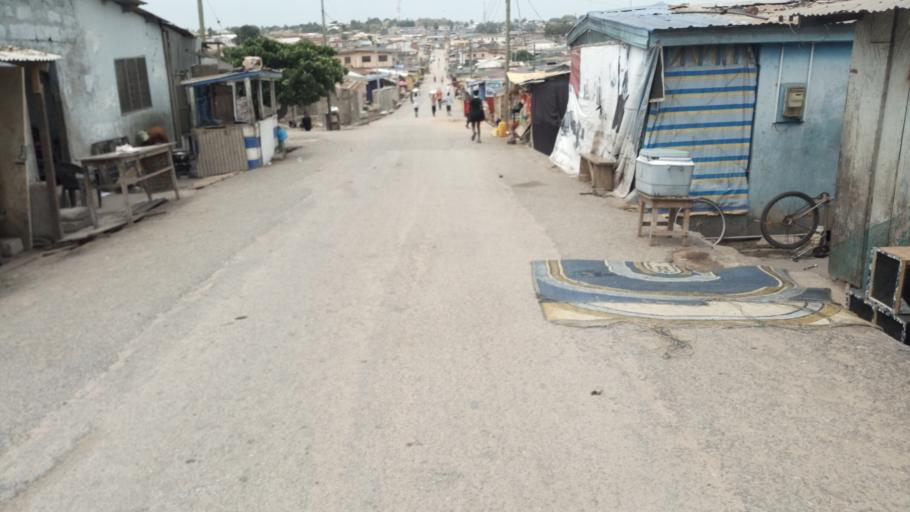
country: GH
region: Central
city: Winneba
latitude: 5.3440
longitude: -0.6213
